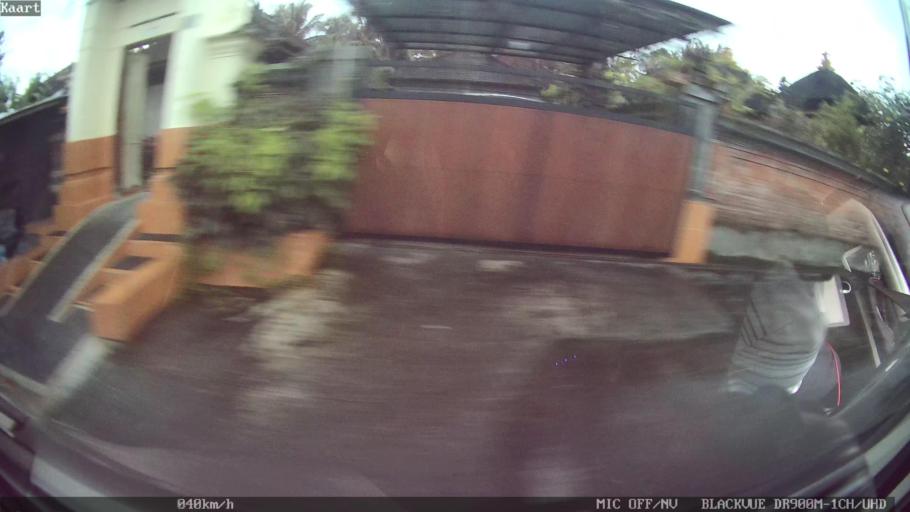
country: ID
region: Bali
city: Banjar Teguan
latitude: -8.5203
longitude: 115.2285
